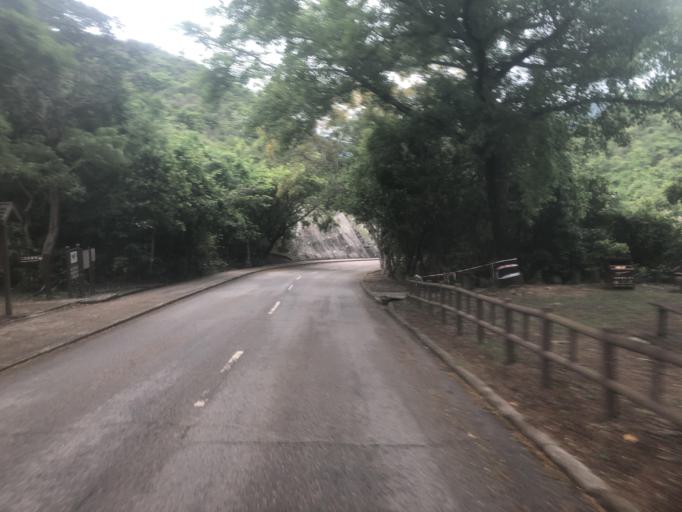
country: HK
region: Sai Kung
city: Sai Kung
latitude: 22.3978
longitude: 114.3260
